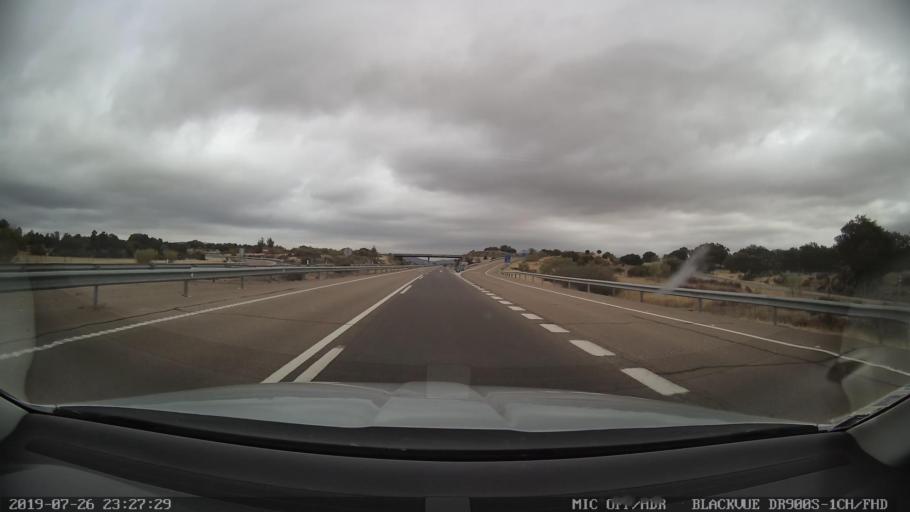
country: ES
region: Extremadura
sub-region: Provincia de Caceres
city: Villamesias
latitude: 39.2275
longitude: -5.8835
